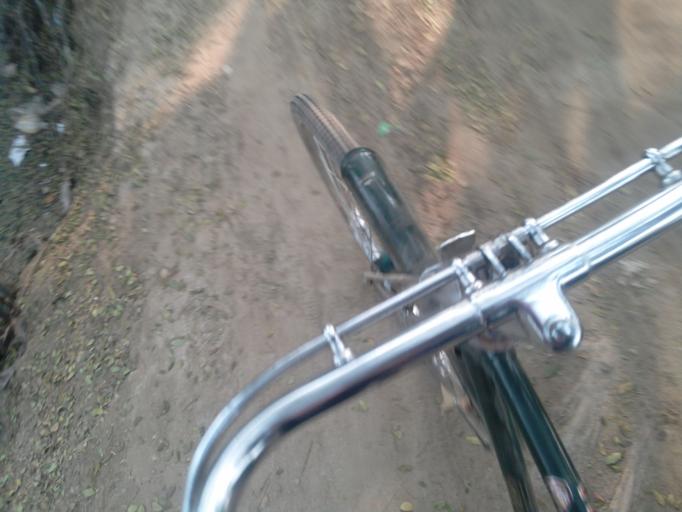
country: BD
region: Khulna
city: Kesabpur
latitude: 22.7673
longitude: 89.2285
